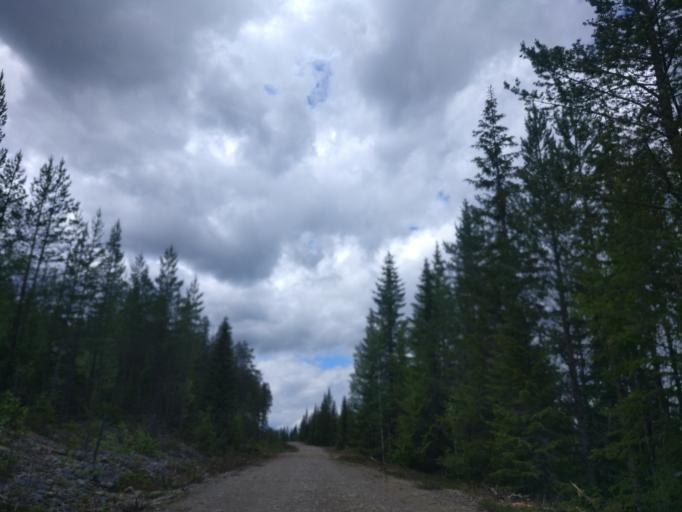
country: SE
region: Jaemtland
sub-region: Harjedalens Kommun
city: Sveg
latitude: 62.1975
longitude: 13.4105
